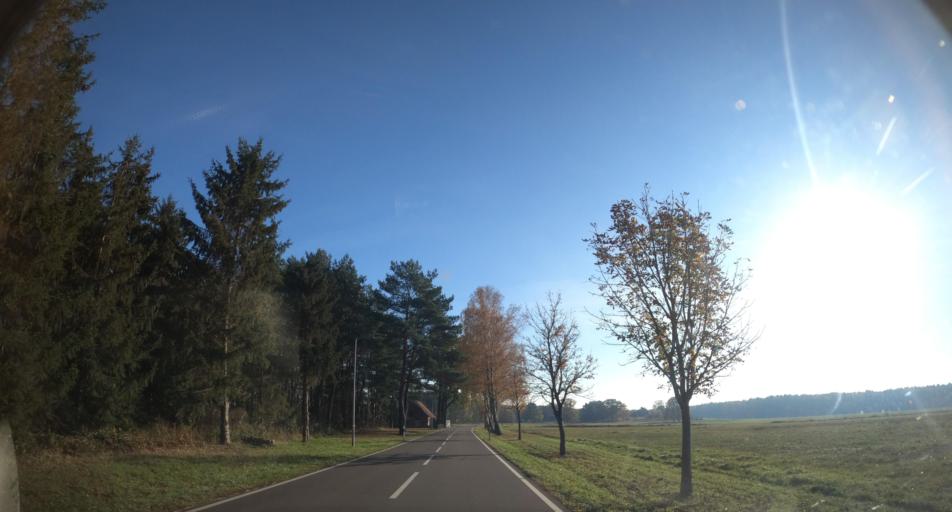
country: DE
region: Mecklenburg-Vorpommern
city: Ahlbeck
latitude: 53.6320
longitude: 14.2247
